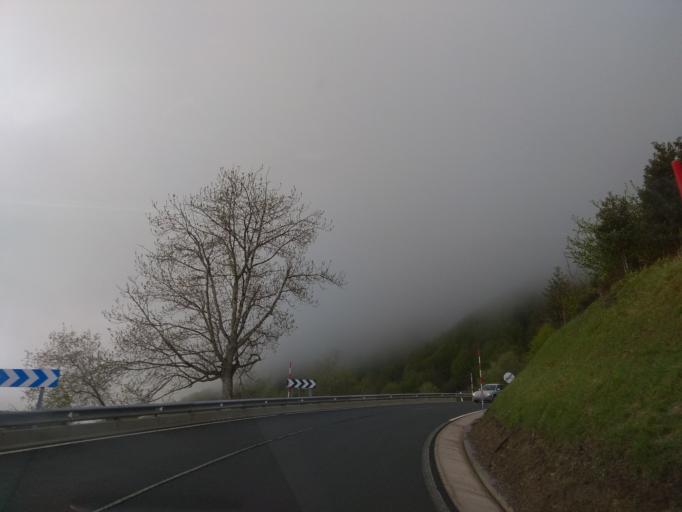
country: ES
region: Basque Country
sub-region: Bizkaia
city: Lanestosa
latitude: 43.1597
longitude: -3.4550
